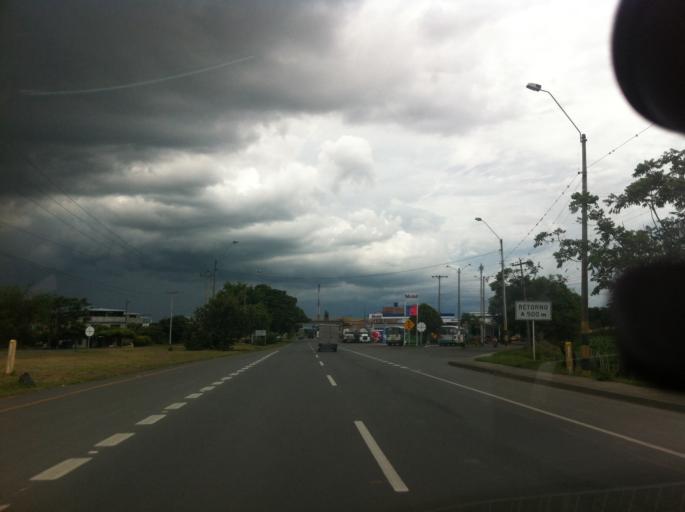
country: CO
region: Valle del Cauca
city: El Cerrito
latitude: 3.6968
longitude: -76.3162
